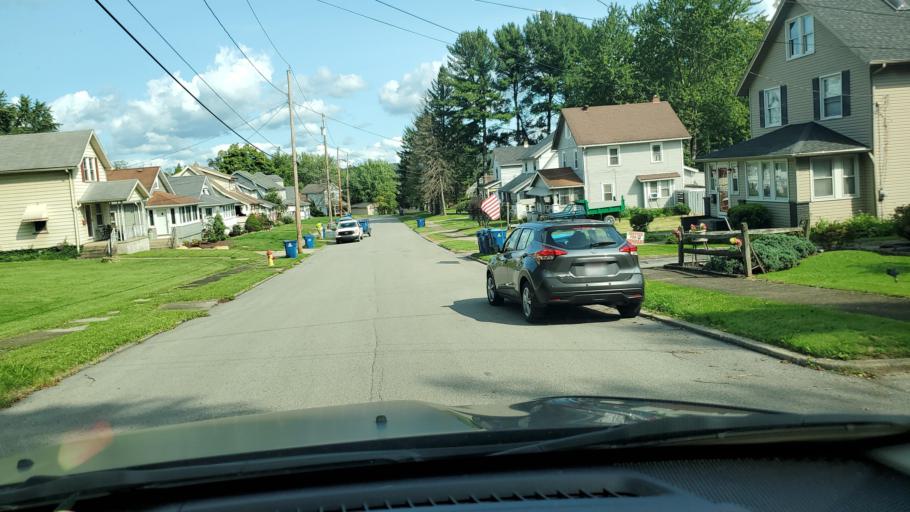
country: US
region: Ohio
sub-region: Mahoning County
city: Struthers
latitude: 41.0514
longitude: -80.5874
